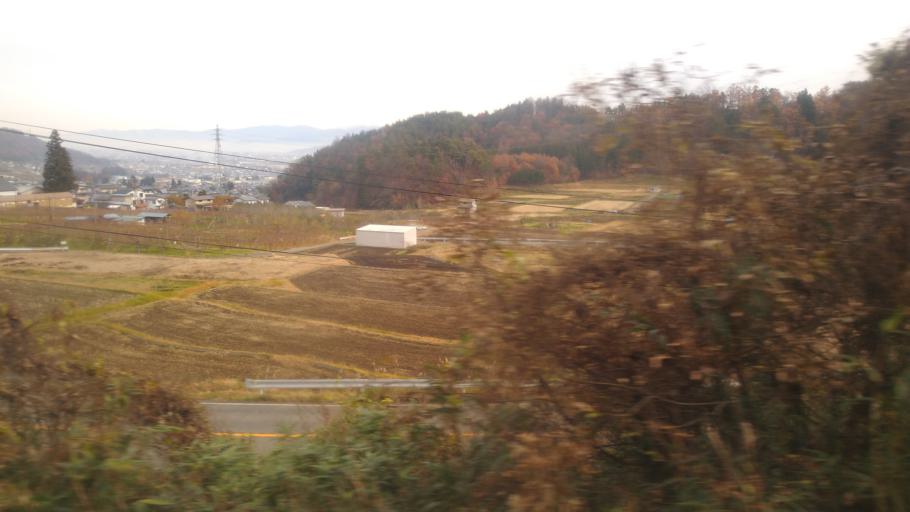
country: JP
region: Nagano
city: Nagano-shi
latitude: 36.5144
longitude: 138.0744
